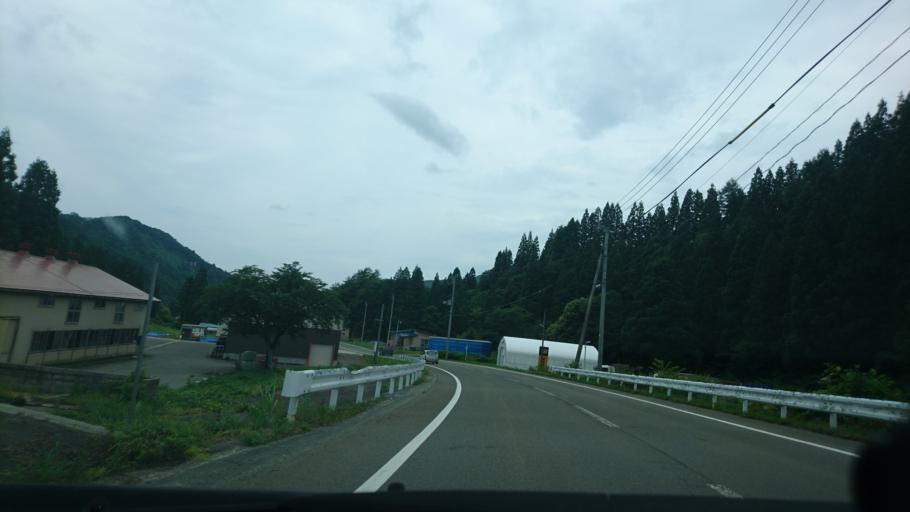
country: JP
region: Akita
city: Yuzawa
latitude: 39.1732
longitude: 140.7223
